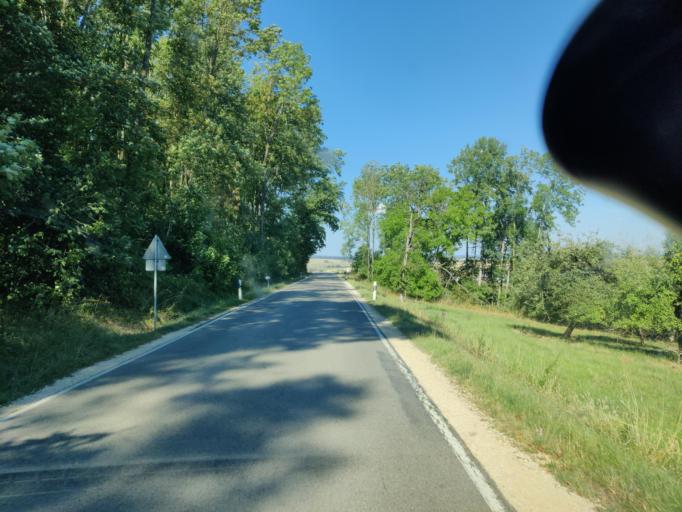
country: DE
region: Bavaria
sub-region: Regierungsbezirk Mittelfranken
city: Ettenstatt
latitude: 49.0748
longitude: 11.0761
